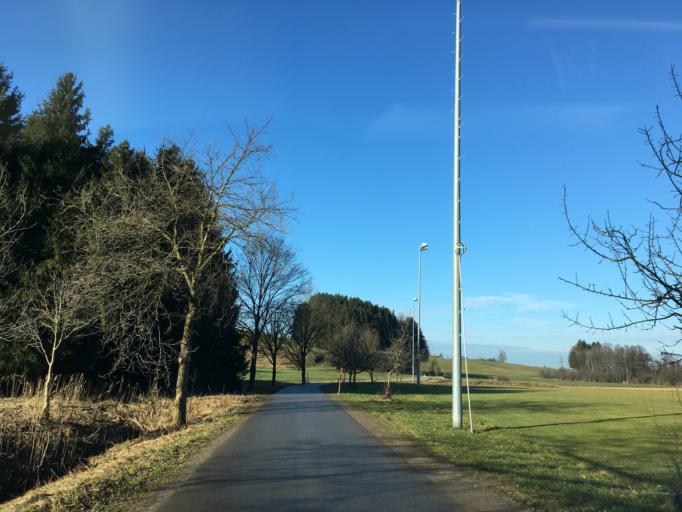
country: DE
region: Bavaria
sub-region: Upper Bavaria
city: Riedering
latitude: 47.8301
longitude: 12.2084
